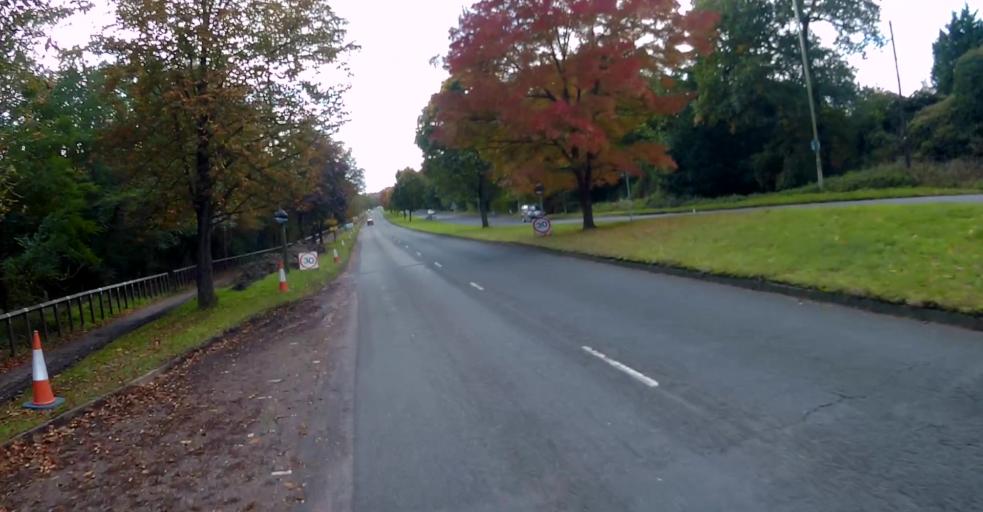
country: GB
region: England
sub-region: Hampshire
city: Aldershot
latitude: 51.2667
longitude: -0.7623
